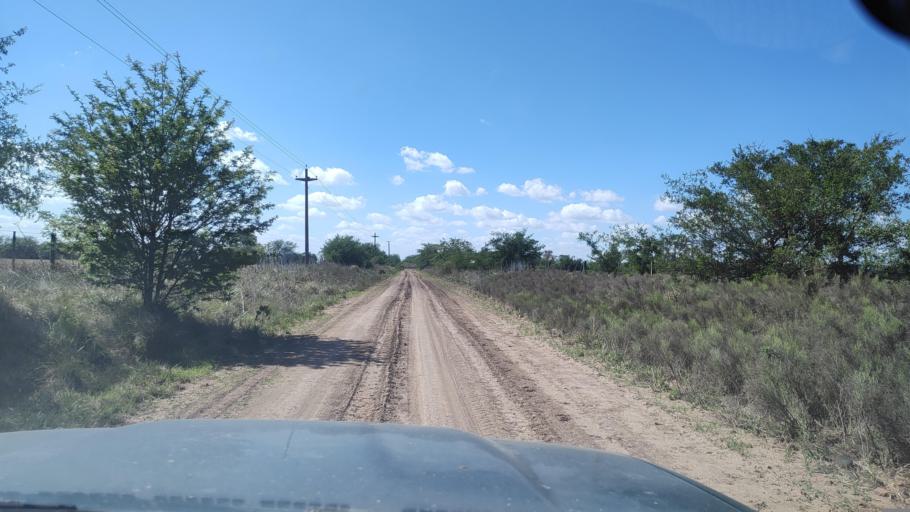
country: AR
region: Buenos Aires
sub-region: Partido de Lujan
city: Lujan
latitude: -34.5252
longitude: -59.1552
